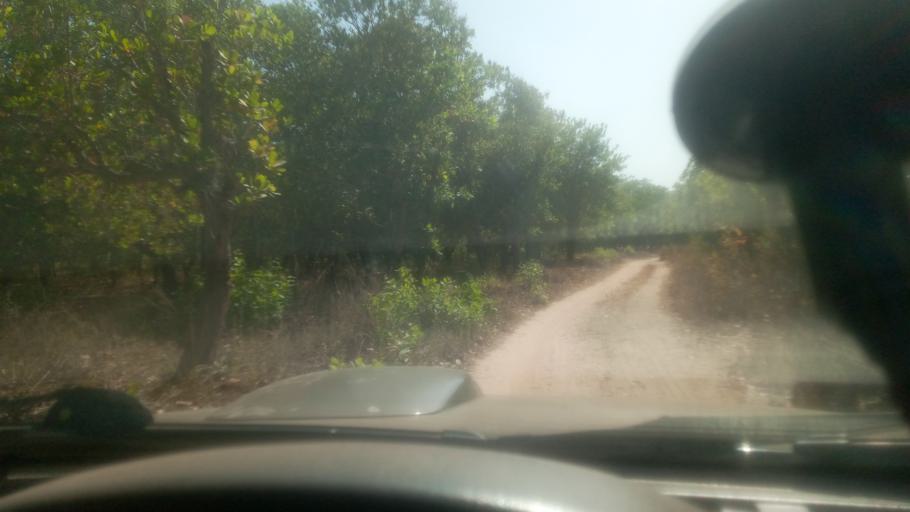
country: GW
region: Oio
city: Farim
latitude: 12.4530
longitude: -15.4203
